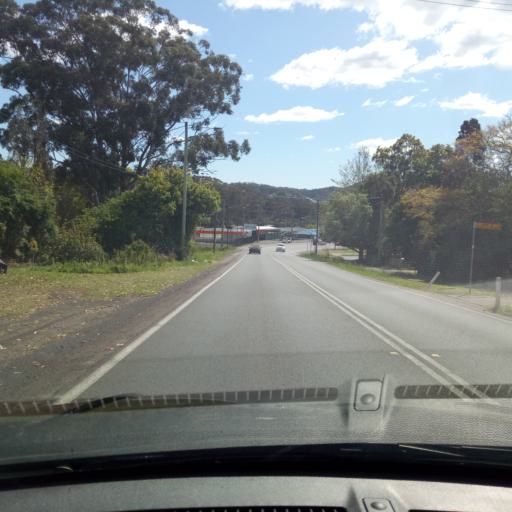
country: AU
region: New South Wales
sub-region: Gosford Shire
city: Gosford
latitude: -33.4131
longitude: 151.3448
